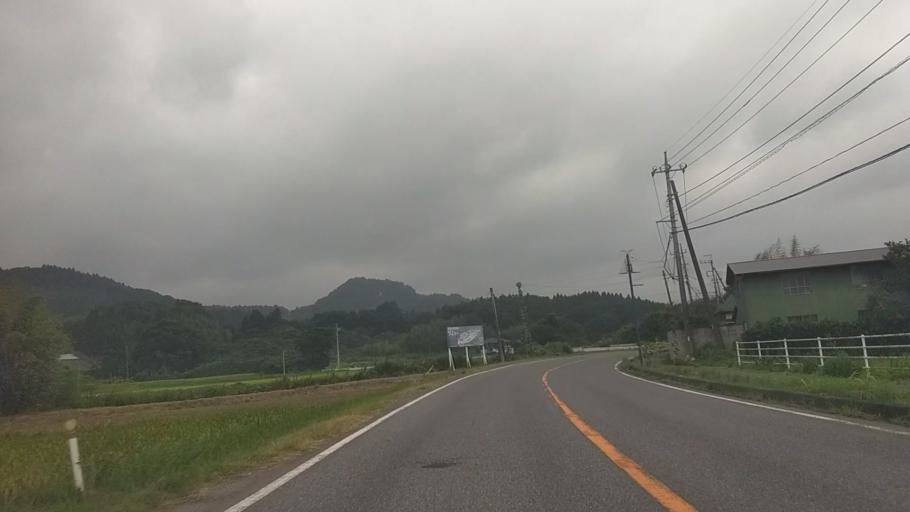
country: JP
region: Chiba
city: Kawaguchi
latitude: 35.1370
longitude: 139.9819
